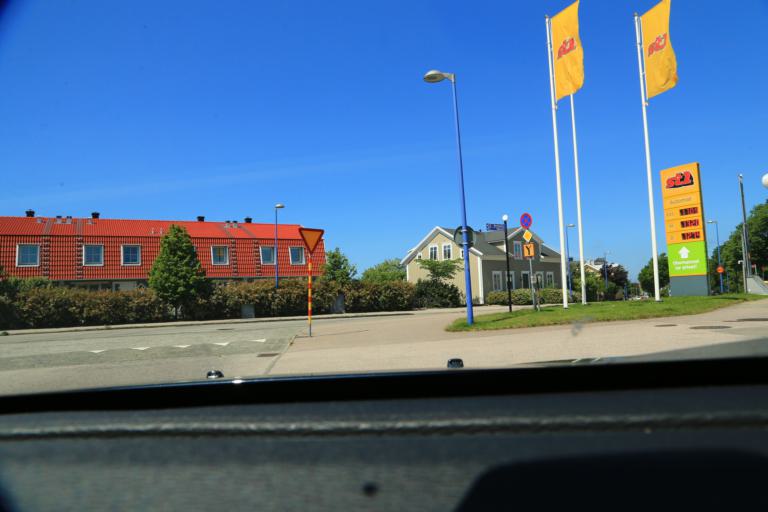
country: SE
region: Halland
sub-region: Varbergs Kommun
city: Varberg
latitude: 57.0990
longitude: 12.2526
